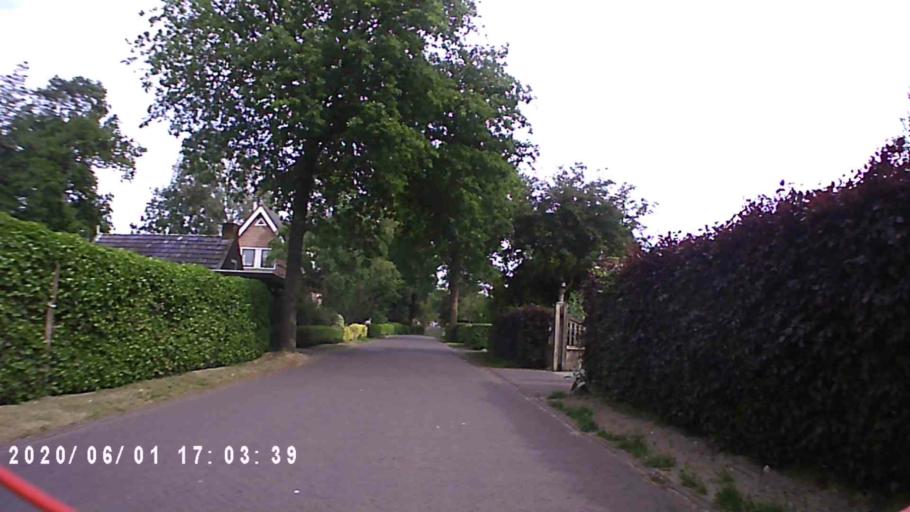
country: NL
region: Friesland
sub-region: Gemeente Tytsjerksteradiel
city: Garyp
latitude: 53.1764
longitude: 5.9314
